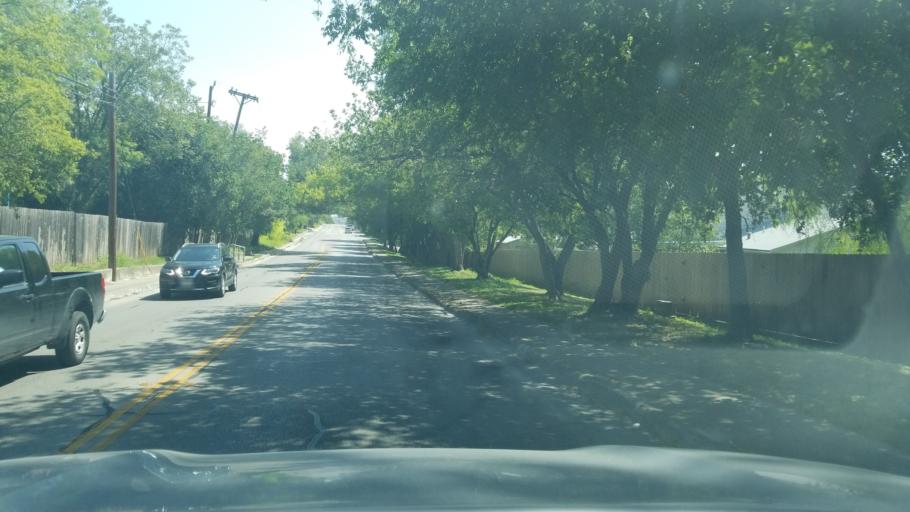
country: US
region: Texas
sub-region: Bexar County
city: Hollywood Park
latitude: 29.5724
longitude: -98.4710
